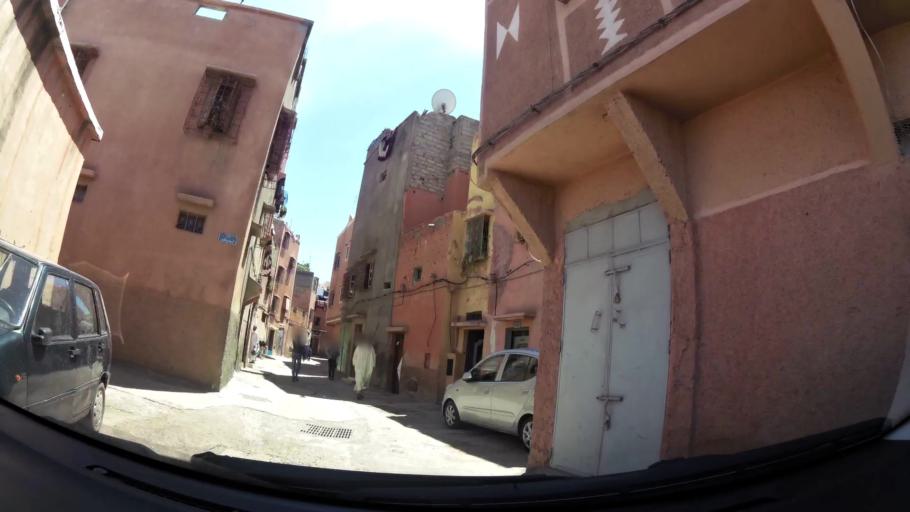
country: MA
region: Marrakech-Tensift-Al Haouz
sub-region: Marrakech
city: Marrakesh
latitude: 31.6213
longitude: -7.9686
